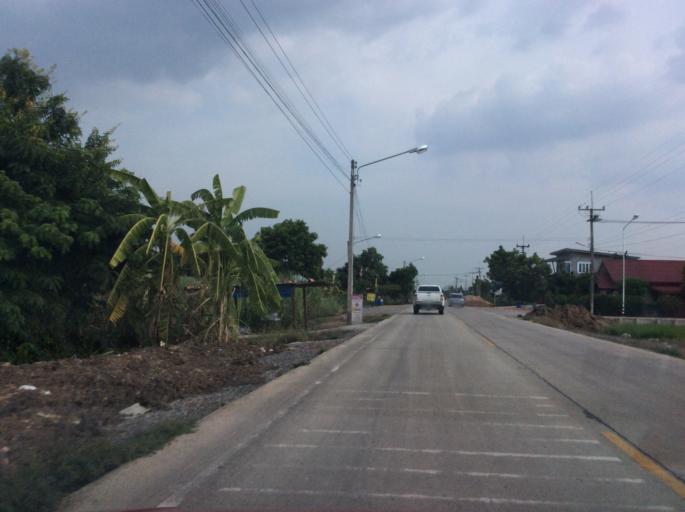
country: TH
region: Pathum Thani
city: Lam Luk Ka
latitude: 13.9701
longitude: 100.7261
